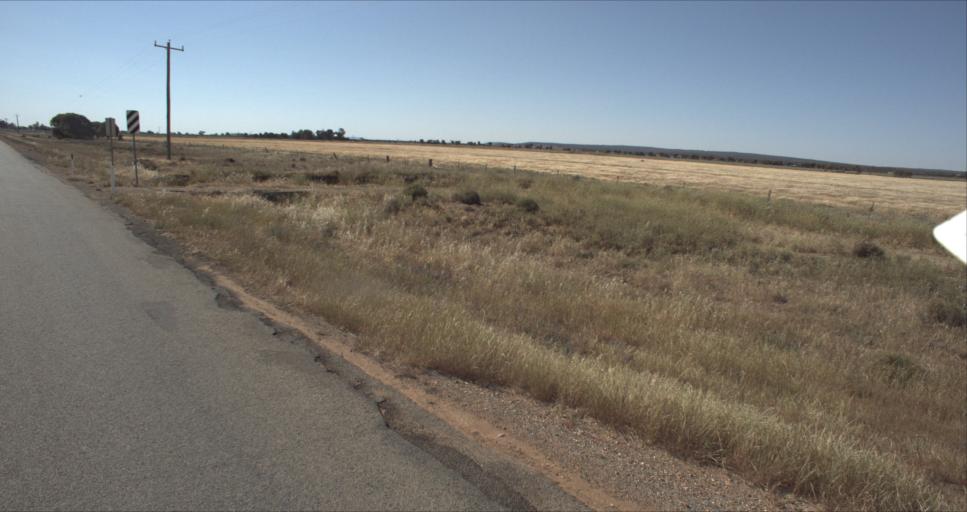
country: AU
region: New South Wales
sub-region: Leeton
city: Leeton
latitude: -34.4902
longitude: 146.3823
